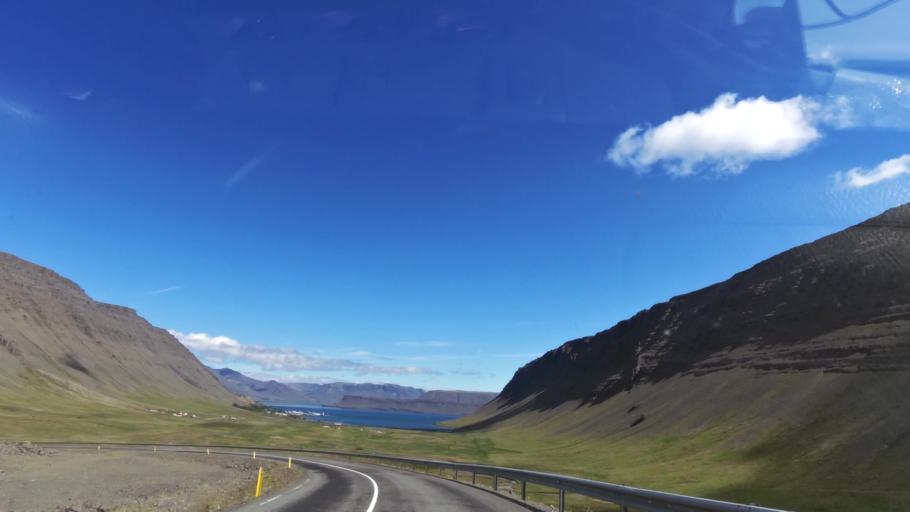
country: IS
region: Westfjords
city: Isafjoerdur
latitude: 65.6610
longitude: -23.6397
